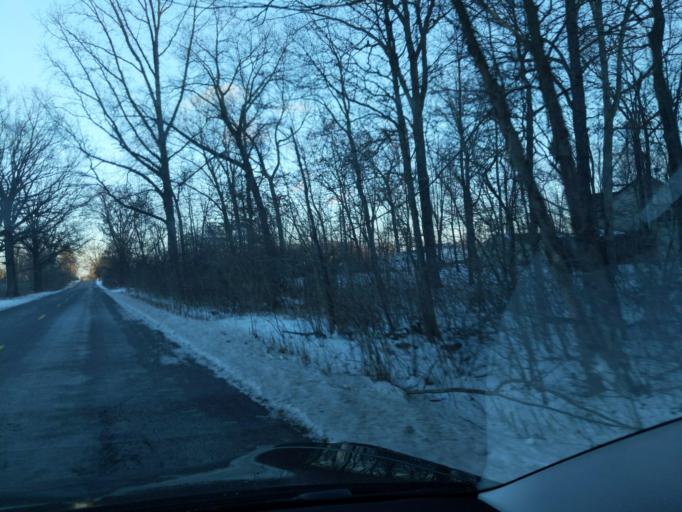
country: US
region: Michigan
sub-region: Ingham County
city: Stockbridge
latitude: 42.4613
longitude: -84.2356
